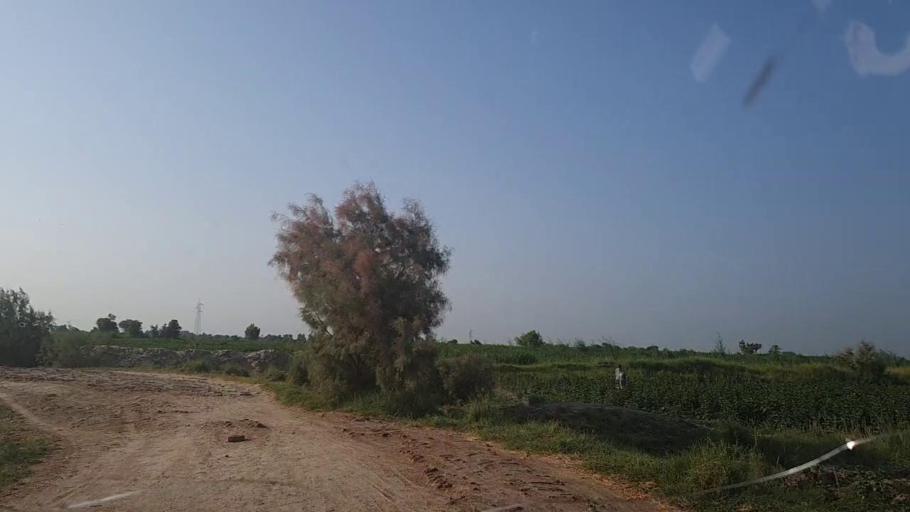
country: PK
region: Sindh
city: Khanpur
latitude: 27.7289
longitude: 69.3068
